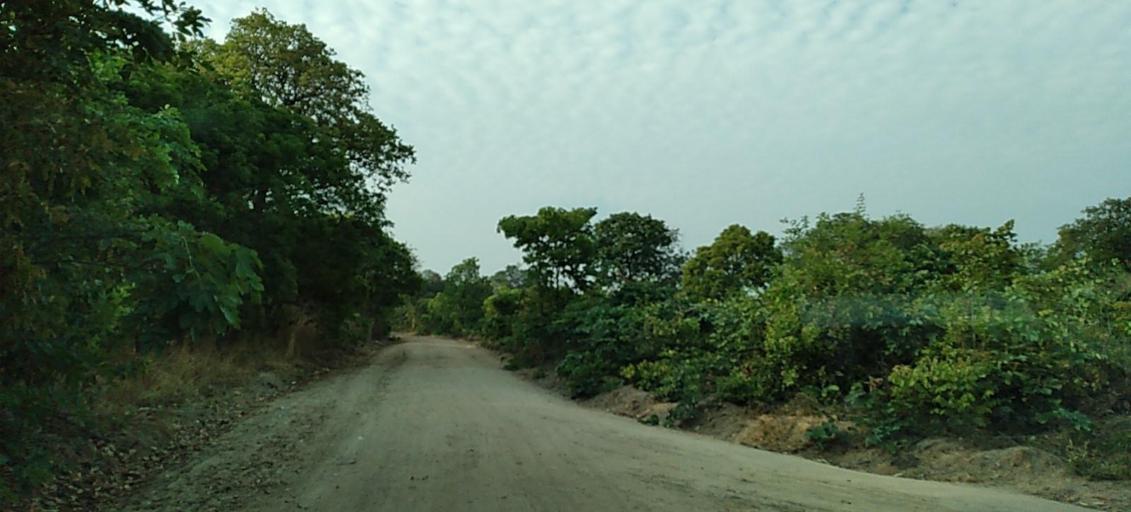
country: ZM
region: Copperbelt
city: Chingola
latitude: -12.8659
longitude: 27.6867
